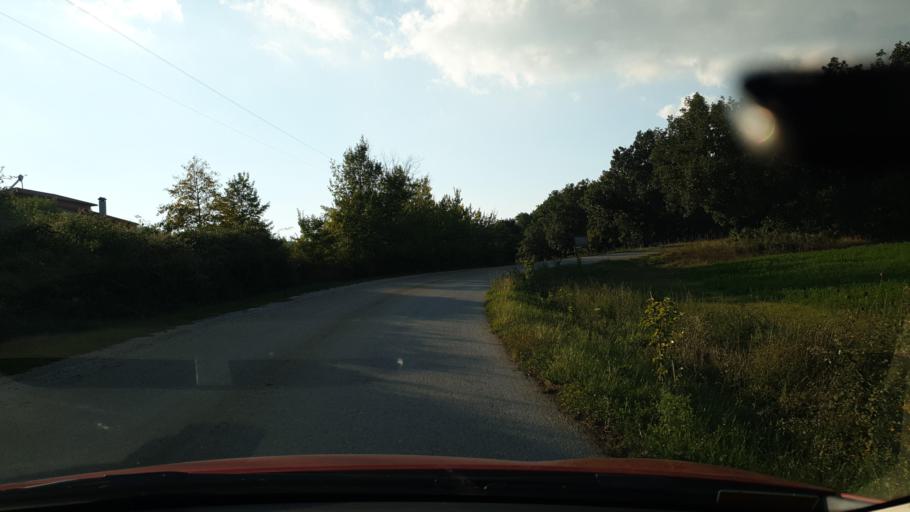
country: GR
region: Central Macedonia
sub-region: Nomos Chalkidikis
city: Galatista
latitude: 40.5227
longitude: 23.2783
